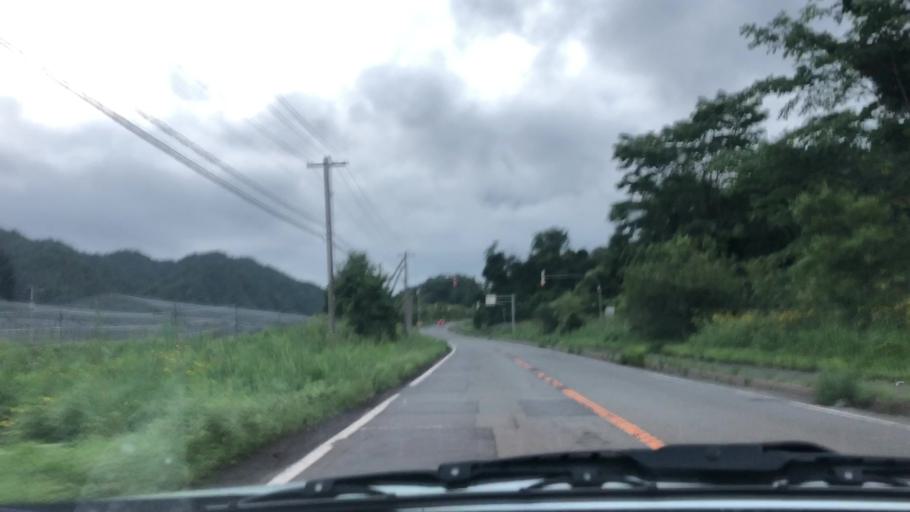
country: JP
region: Hokkaido
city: Chitose
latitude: 42.9062
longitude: 141.9928
